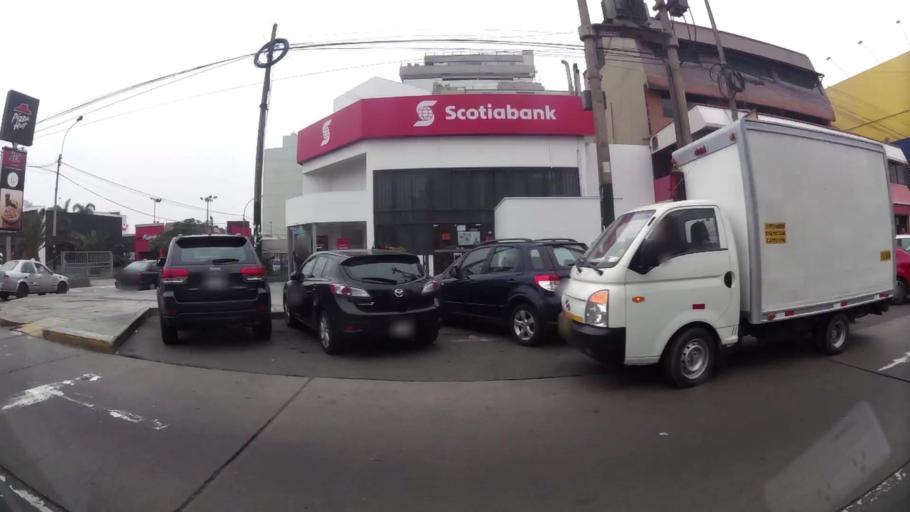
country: PE
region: Lima
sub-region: Lima
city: Surco
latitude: -12.1295
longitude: -76.9833
